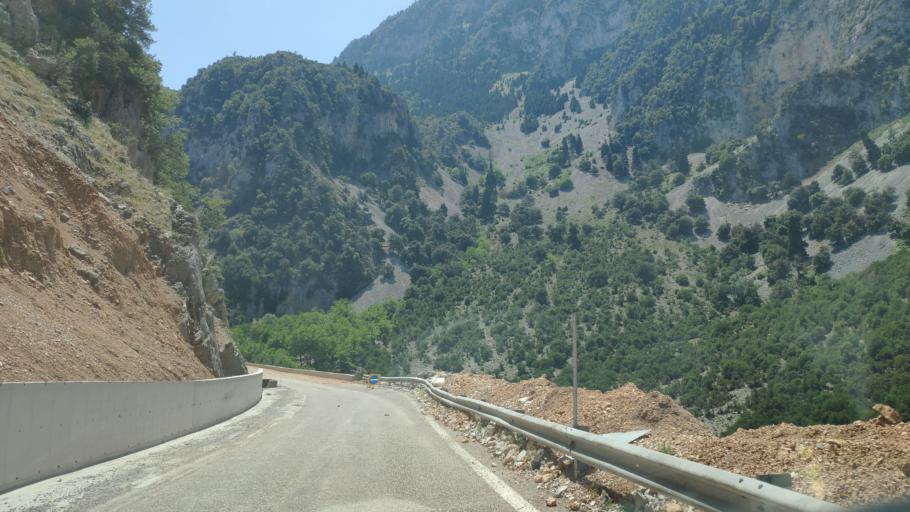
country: GR
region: West Greece
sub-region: Nomos Aitolias kai Akarnanias
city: Krikellos
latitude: 39.0068
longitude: 21.3685
